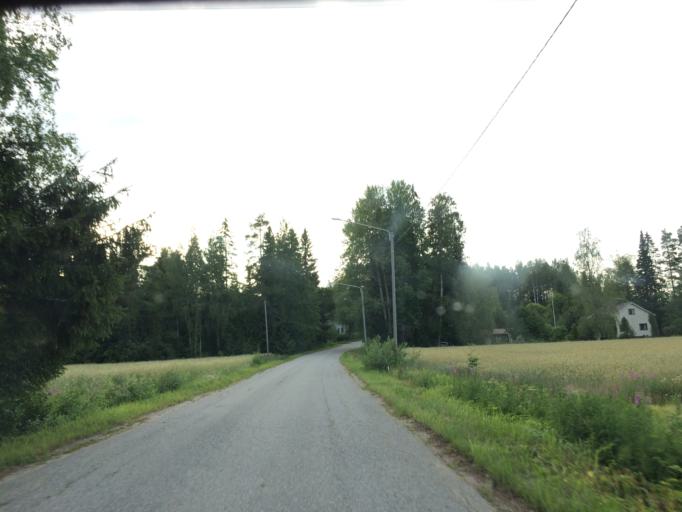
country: FI
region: Haeme
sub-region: Haemeenlinna
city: Tervakoski
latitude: 60.8494
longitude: 24.6227
